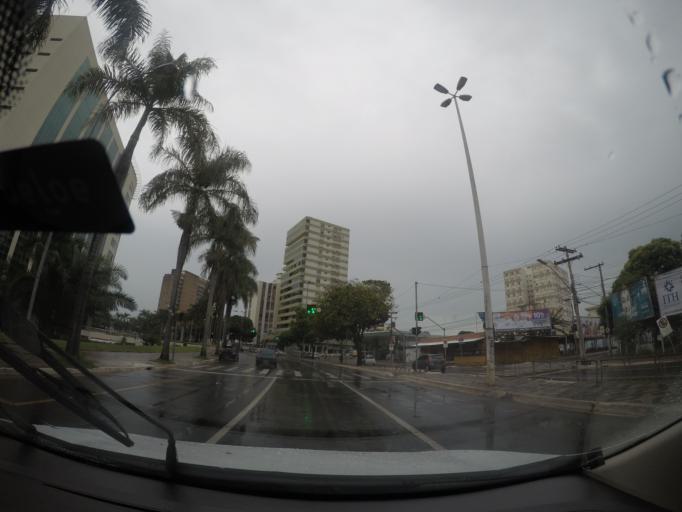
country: BR
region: Goias
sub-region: Goiania
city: Goiania
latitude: -16.6824
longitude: -49.2567
